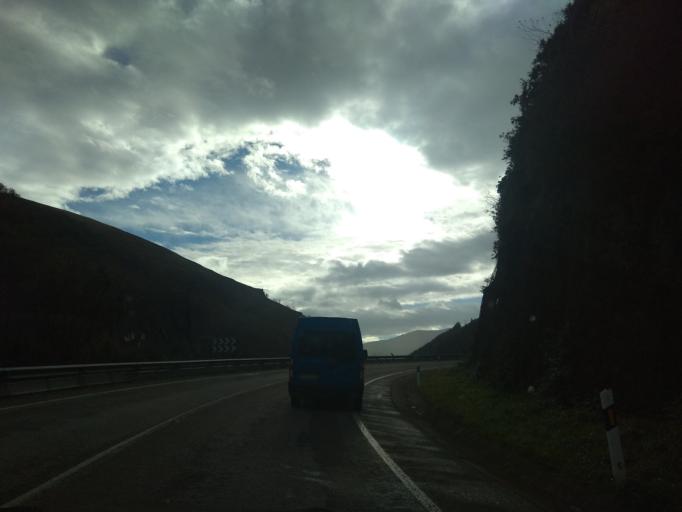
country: ES
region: Cantabria
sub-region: Provincia de Cantabria
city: San Pedro del Romeral
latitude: 43.1411
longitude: -3.8998
